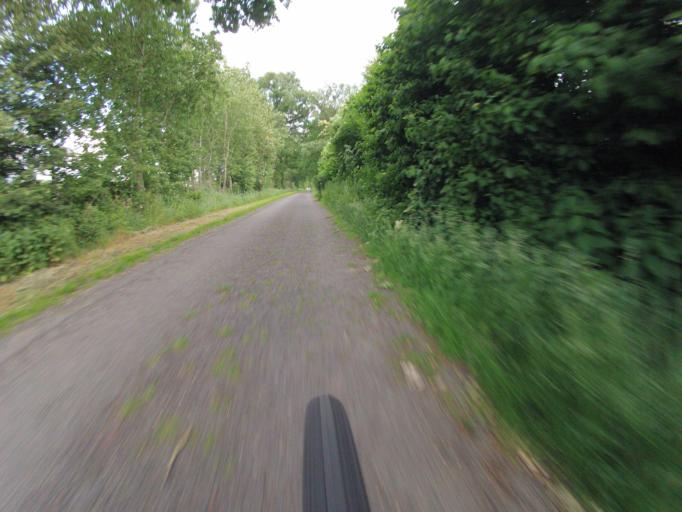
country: DE
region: North Rhine-Westphalia
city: Ibbenburen
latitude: 52.2919
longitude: 7.6854
